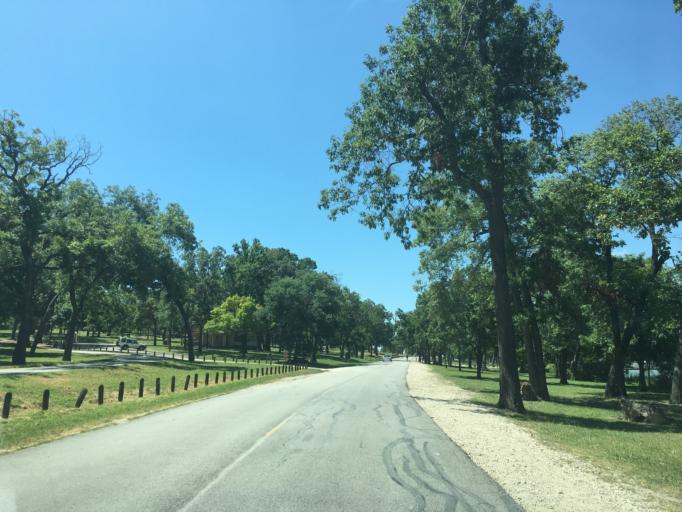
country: US
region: Texas
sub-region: Dallas County
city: Highland Park
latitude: 32.8476
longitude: -96.7166
